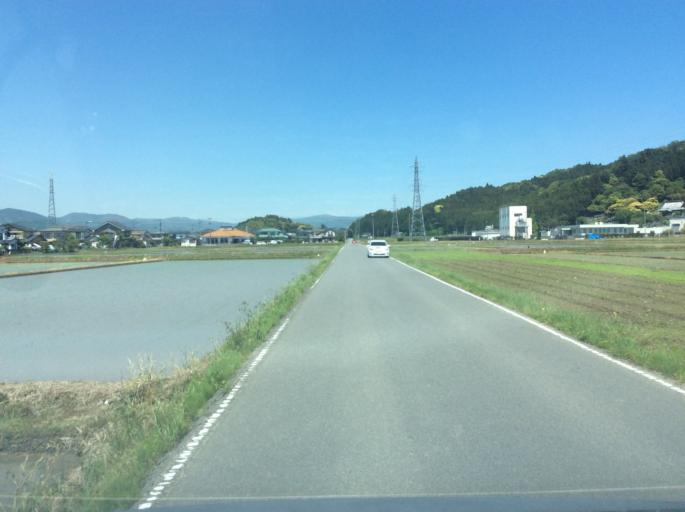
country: JP
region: Fukushima
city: Iwaki
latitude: 37.0749
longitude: 140.8862
